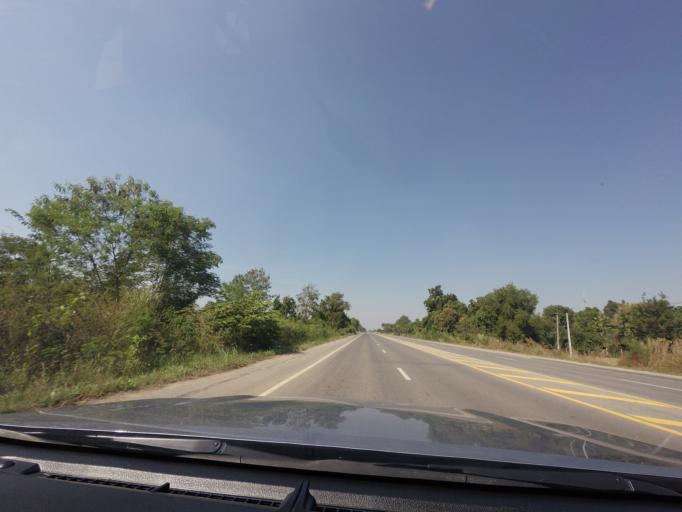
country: TH
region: Sukhothai
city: Ban Na
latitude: 17.0334
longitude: 99.7318
